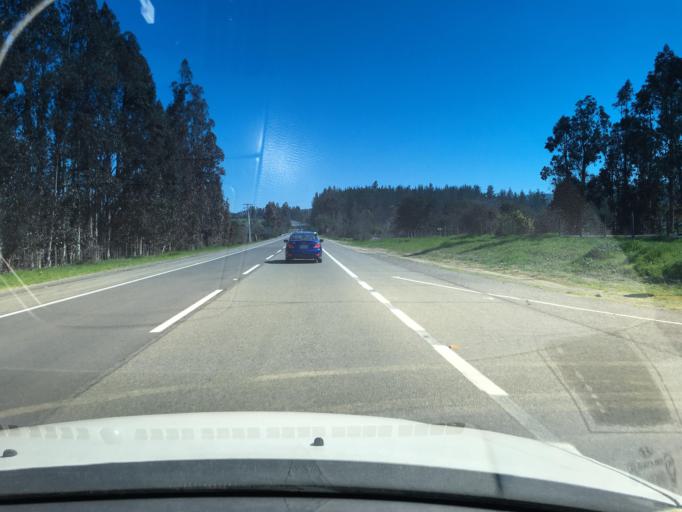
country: CL
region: Valparaiso
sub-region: San Antonio Province
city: El Tabo
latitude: -33.3900
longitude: -71.4737
